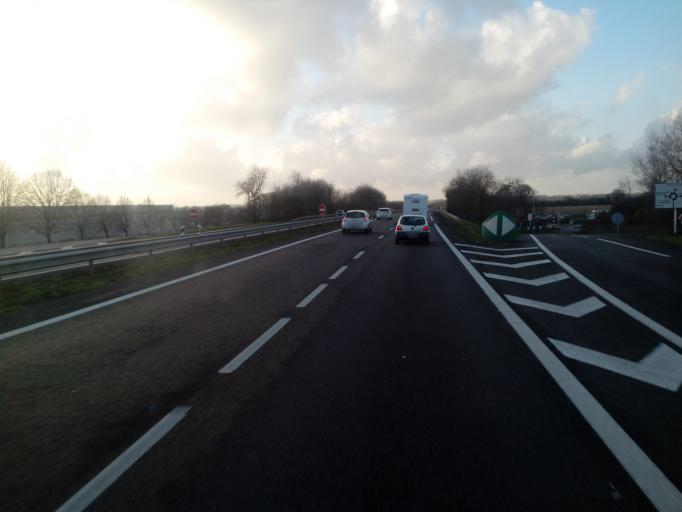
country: FR
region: Pays de la Loire
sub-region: Departement de Maine-et-Loire
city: Saint-Germain-sur-Moine
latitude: 47.1210
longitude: -1.0935
